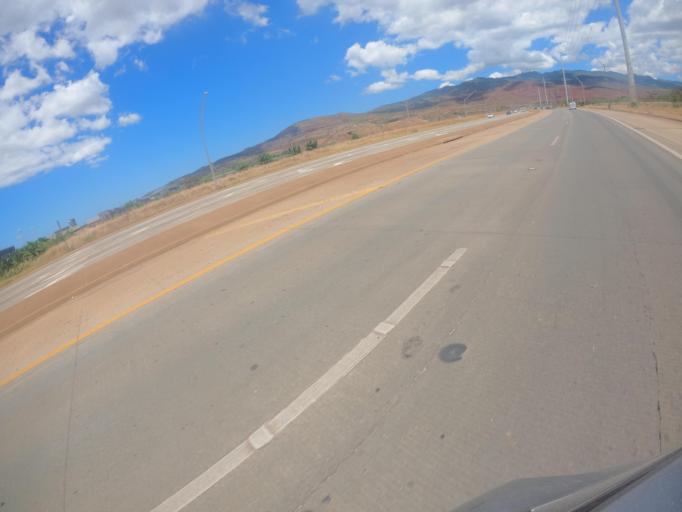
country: US
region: Hawaii
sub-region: Honolulu County
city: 'Ewa Villages
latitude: 21.3593
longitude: -158.0537
